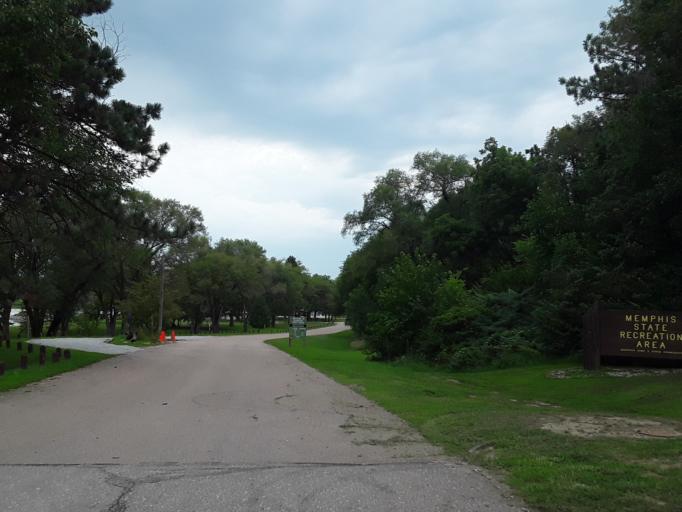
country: US
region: Nebraska
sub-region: Saunders County
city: Ashland
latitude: 41.0958
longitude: -96.4365
